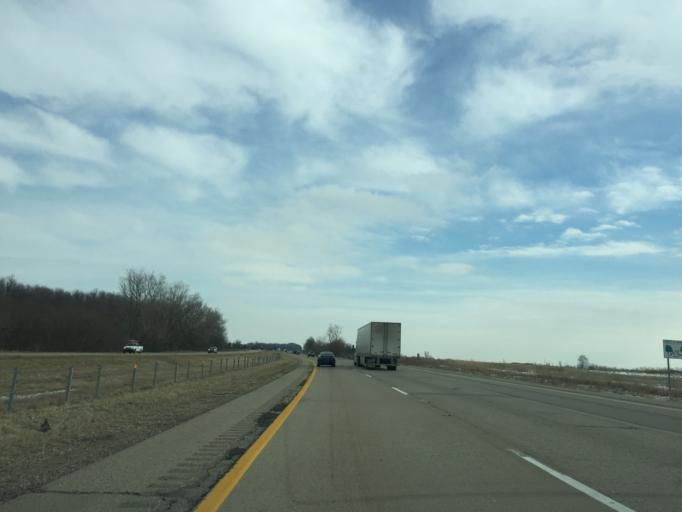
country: US
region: Michigan
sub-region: Ionia County
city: Saranac
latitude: 42.8788
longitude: -85.1522
